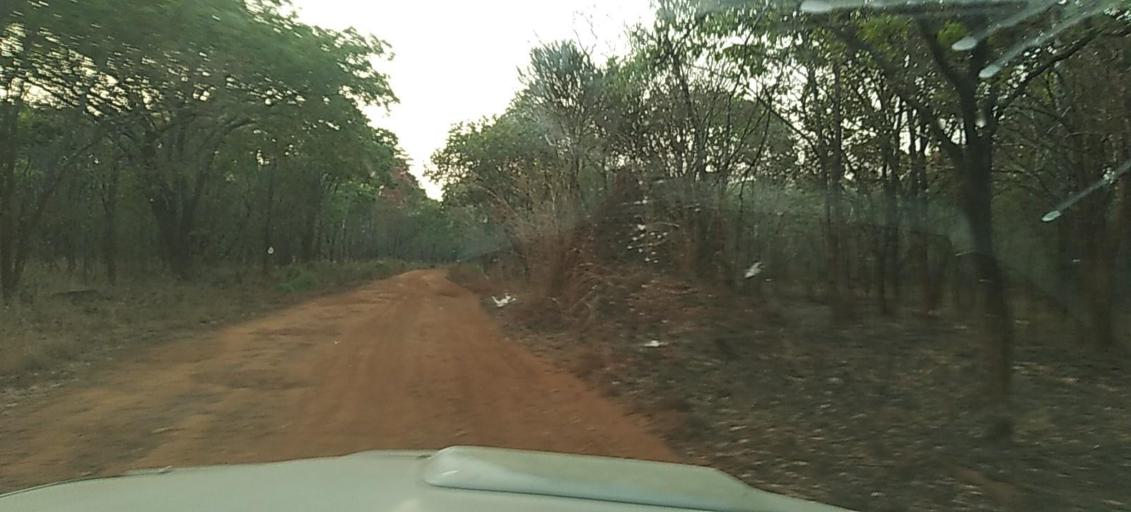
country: ZM
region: North-Western
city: Kasempa
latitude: -13.0861
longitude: 26.3973
